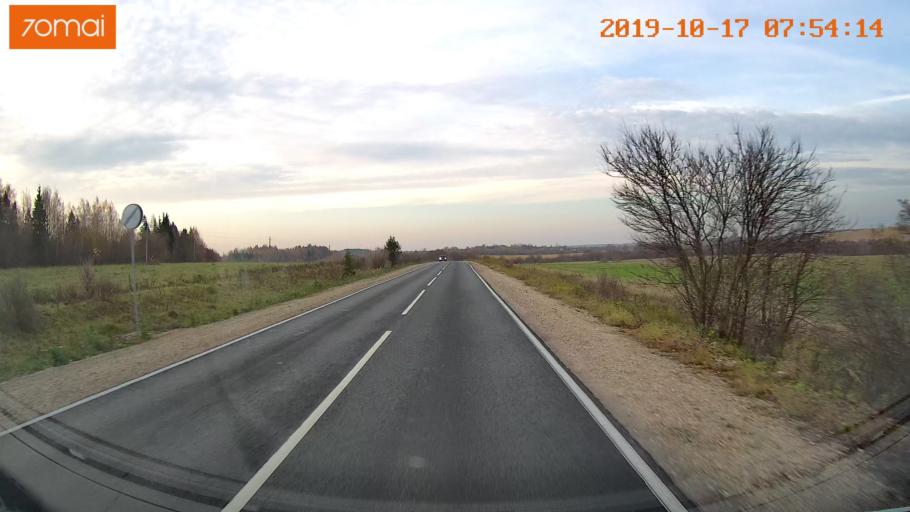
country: RU
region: Vladimir
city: Bavleny
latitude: 56.4522
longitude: 39.6078
